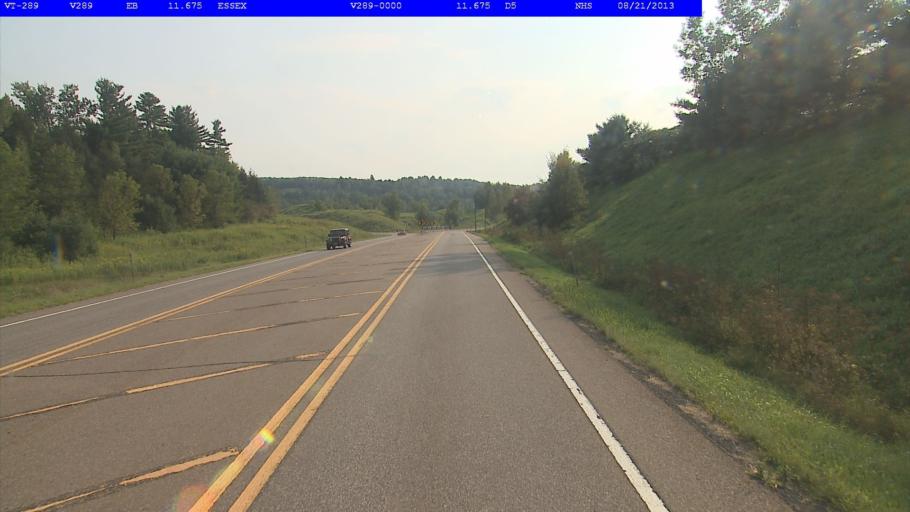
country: US
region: Vermont
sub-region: Chittenden County
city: Essex Junction
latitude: 44.4848
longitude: -73.0662
